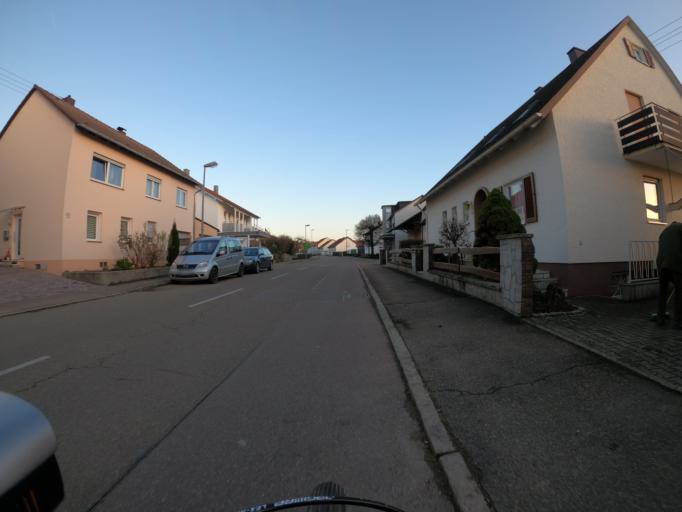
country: DE
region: Baden-Wuerttemberg
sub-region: Regierungsbezirk Stuttgart
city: Schlierbach
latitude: 48.6717
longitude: 9.5243
